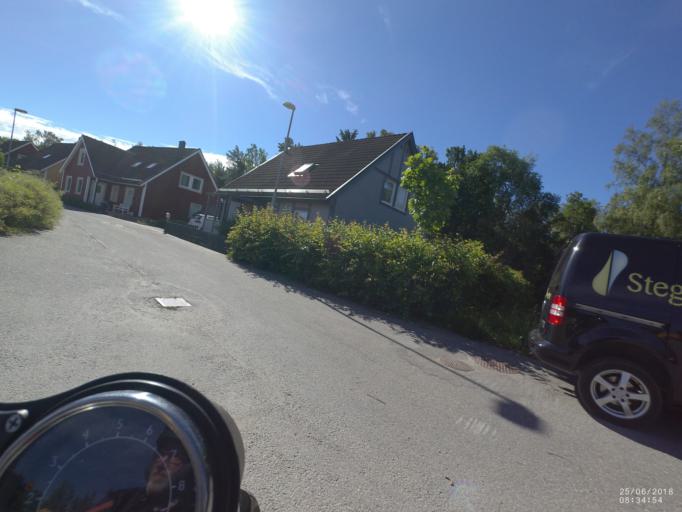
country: SE
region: Soedermanland
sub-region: Nykopings Kommun
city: Nykoping
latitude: 58.7274
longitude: 17.0298
